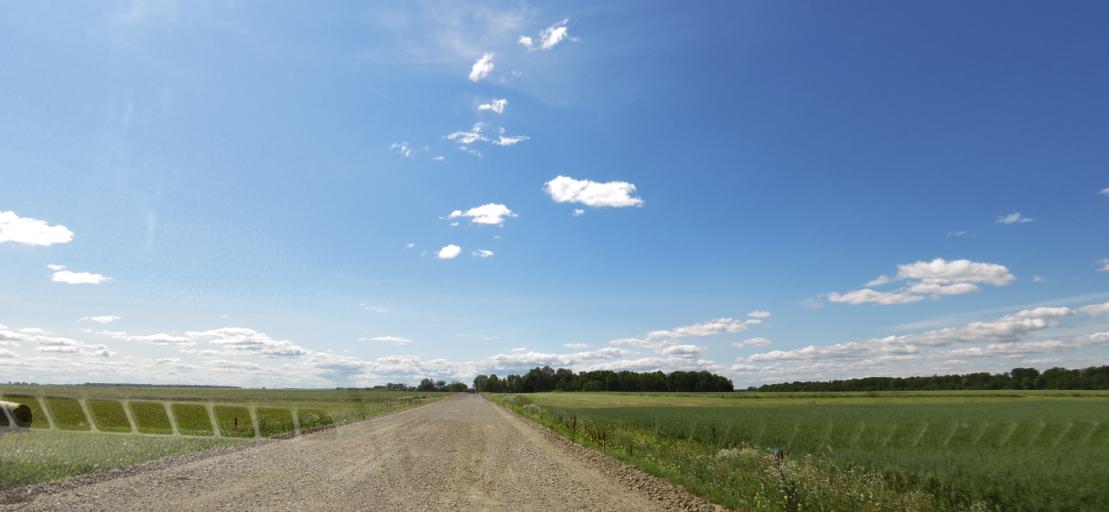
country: LT
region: Panevezys
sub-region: Birzai
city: Birzai
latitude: 56.2957
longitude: 24.6062
